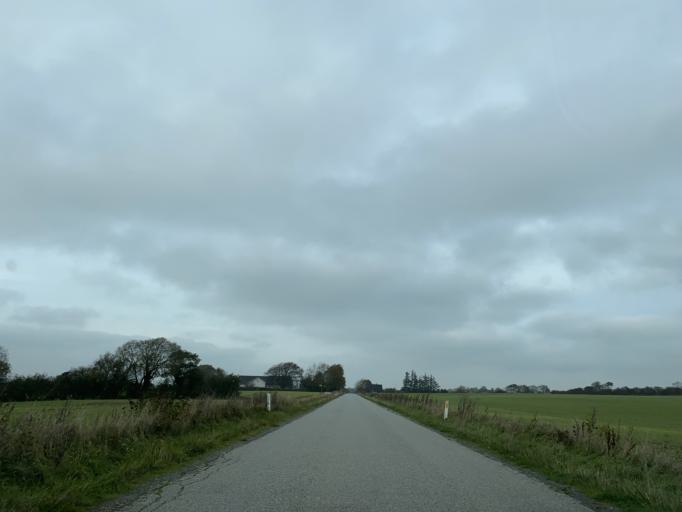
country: DK
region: South Denmark
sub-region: Haderslev Kommune
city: Starup
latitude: 55.1722
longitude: 9.5182
